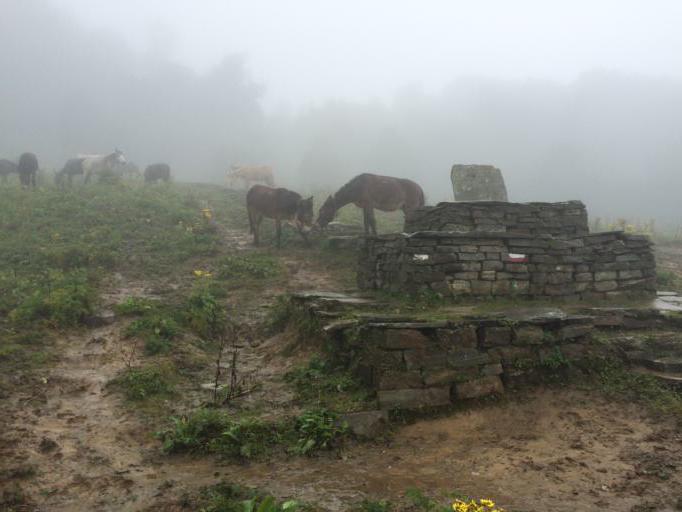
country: NP
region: Western Region
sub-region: Dhawalagiri Zone
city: Chitre
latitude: 28.4000
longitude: 83.7060
